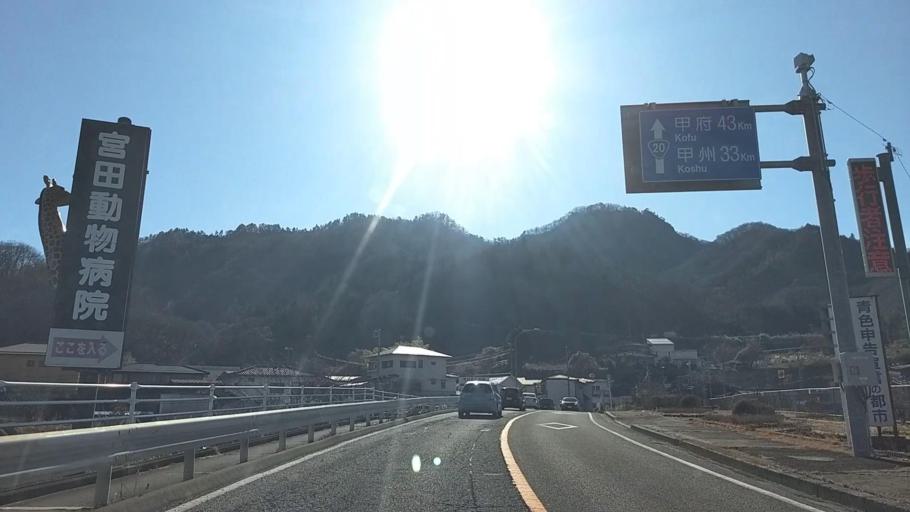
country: JP
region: Yamanashi
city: Otsuki
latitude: 35.6127
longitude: 138.9663
